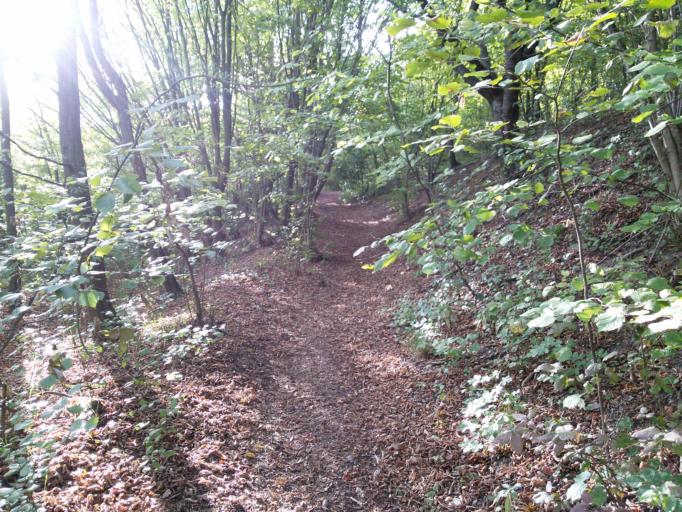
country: CZ
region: South Moravian
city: Boritov
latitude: 49.4505
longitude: 16.5868
